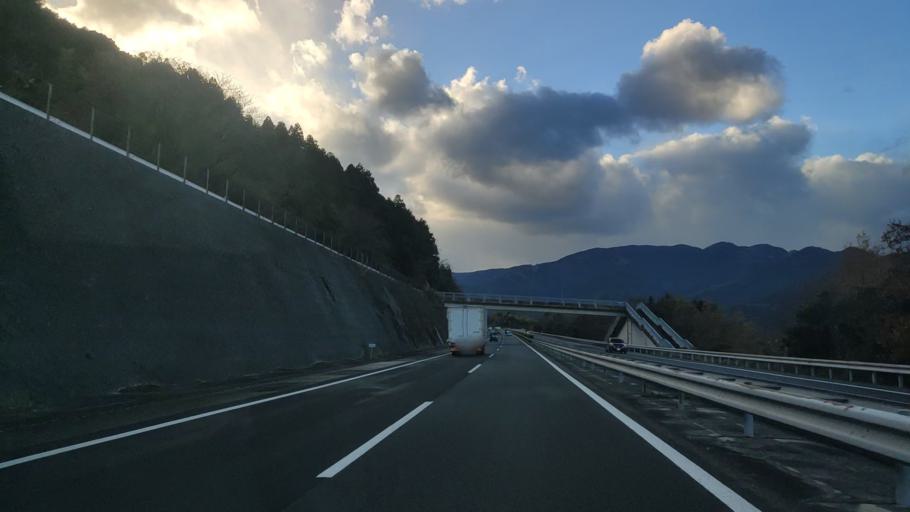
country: JP
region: Ehime
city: Saijo
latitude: 33.8559
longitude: 133.0304
